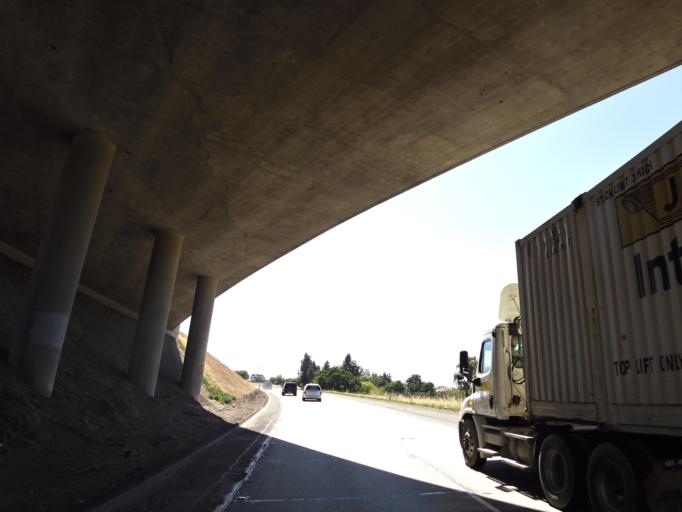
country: US
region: California
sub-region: San Joaquin County
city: Lathrop
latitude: 37.7886
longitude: -121.3023
